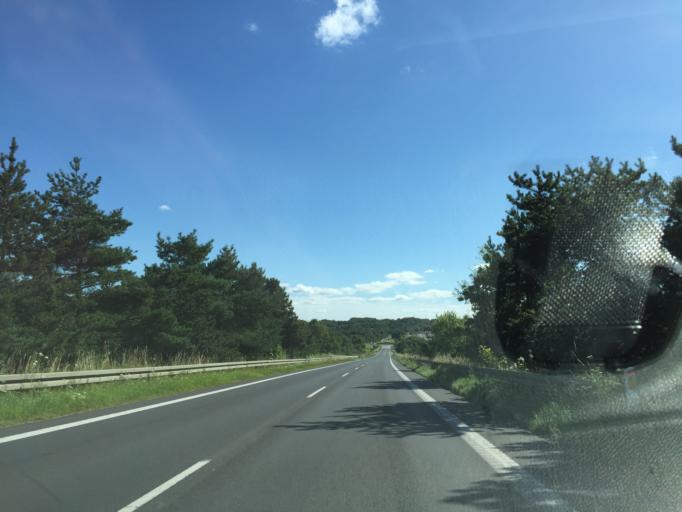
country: DK
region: Central Jutland
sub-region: Viborg Kommune
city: Bjerringbro
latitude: 56.3770
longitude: 9.6775
